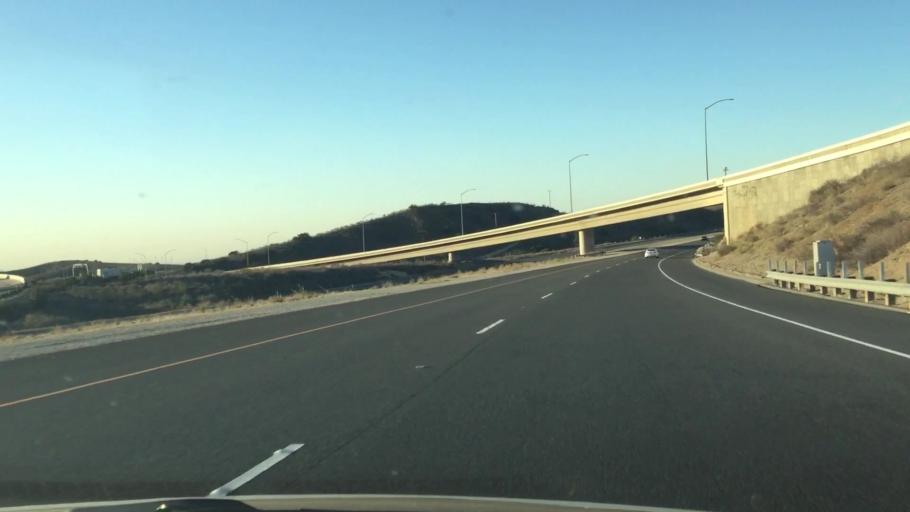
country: US
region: California
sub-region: Orange County
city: Foothill Ranch
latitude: 33.7097
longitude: -117.7187
